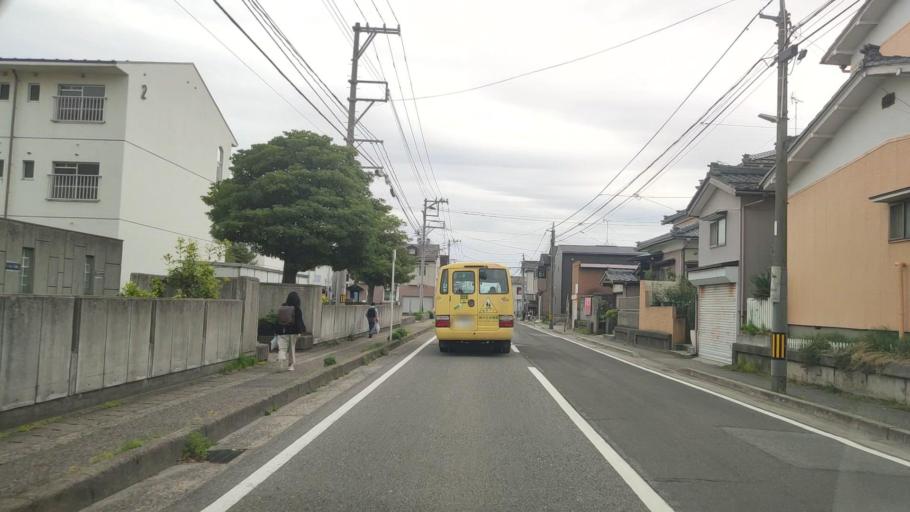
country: JP
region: Niigata
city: Niigata-shi
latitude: 37.9425
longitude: 139.0784
